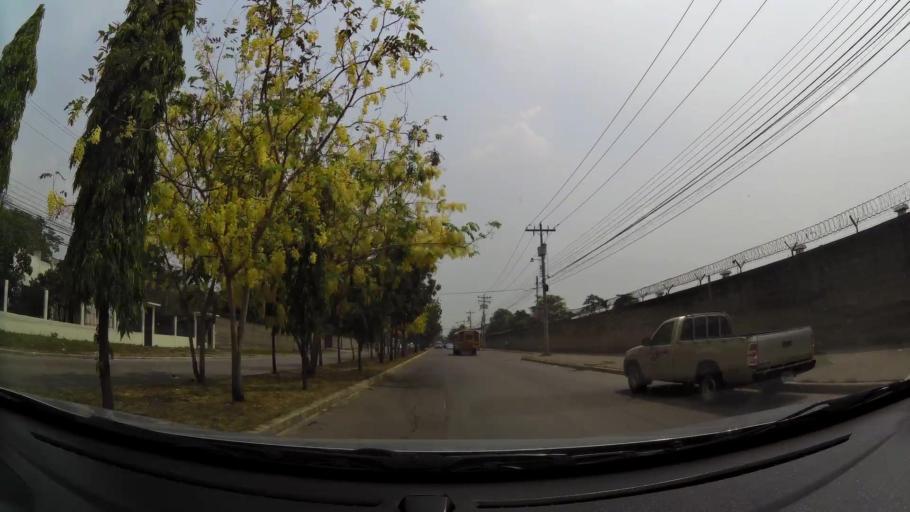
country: HN
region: Cortes
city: San Pedro Sula
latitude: 15.4857
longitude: -88.0245
